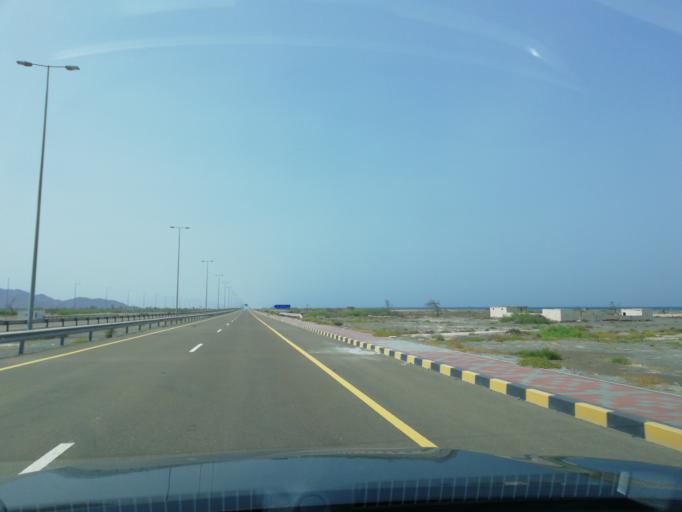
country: AE
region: Al Fujayrah
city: Al Fujayrah
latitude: 24.9304
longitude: 56.3842
